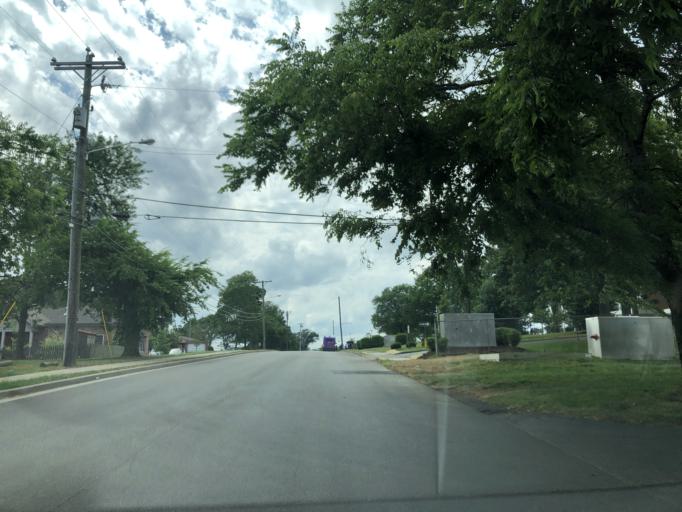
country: US
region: Tennessee
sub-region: Davidson County
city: Goodlettsville
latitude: 36.2673
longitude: -86.6977
